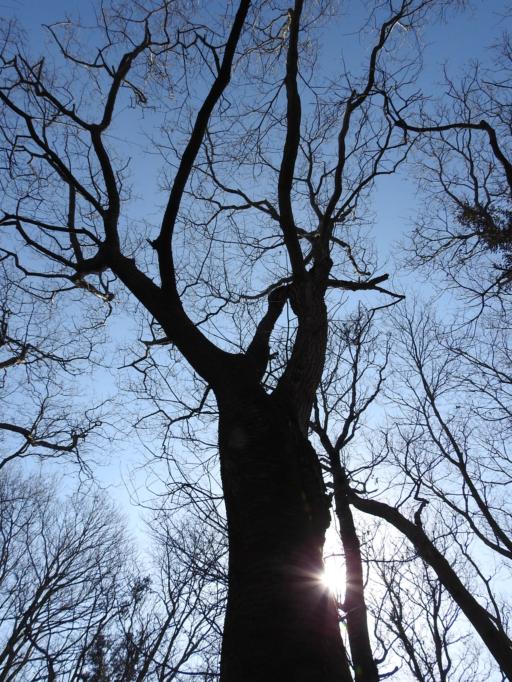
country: JP
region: Ibaraki
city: Tsukuba
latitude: 36.1625
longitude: 140.1368
